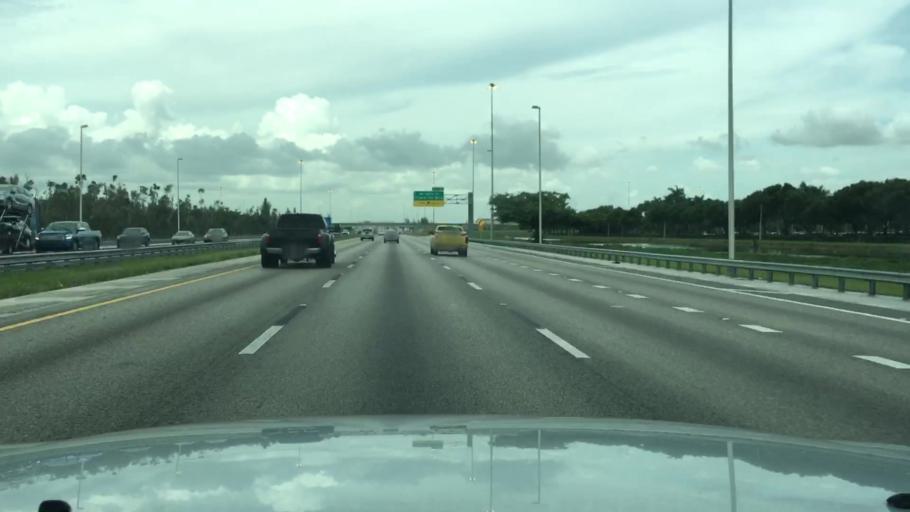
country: US
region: Florida
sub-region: Miami-Dade County
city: Doral
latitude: 25.8577
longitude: -80.3950
